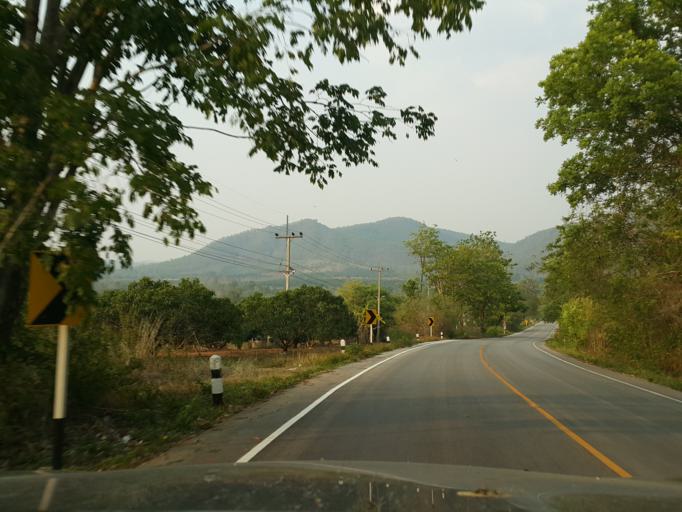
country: TH
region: Lamphun
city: Li
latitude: 17.8428
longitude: 98.9933
